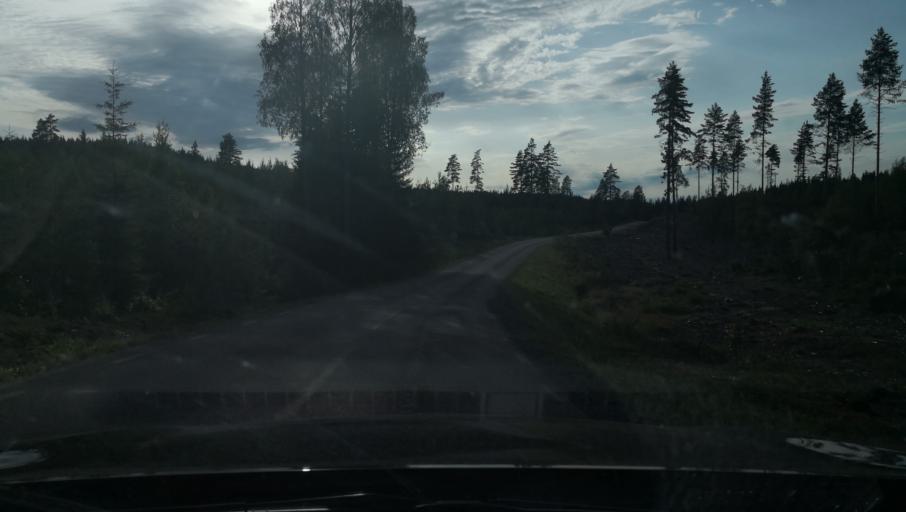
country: SE
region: Dalarna
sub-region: Ludvika Kommun
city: Ludvika
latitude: 60.0414
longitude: 15.2964
